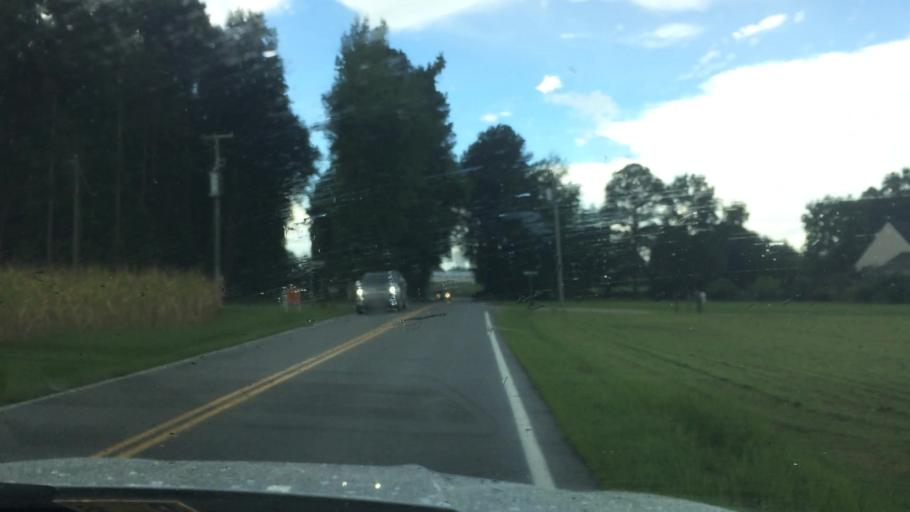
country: US
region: Virginia
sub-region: King William County
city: West Point
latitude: 37.4724
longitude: -76.8269
